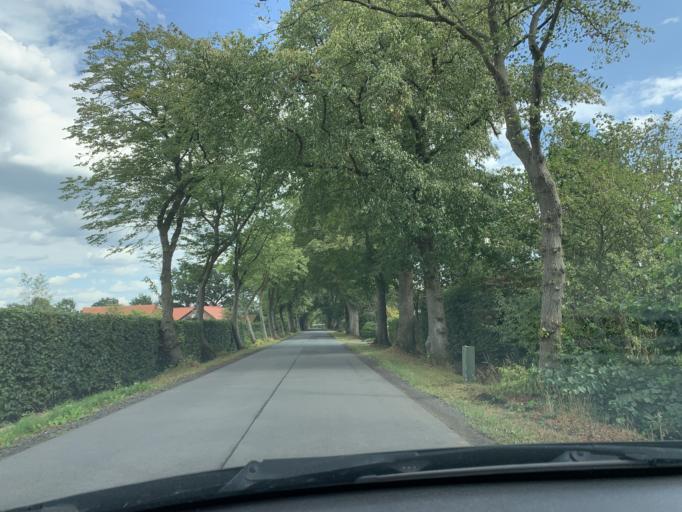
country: DE
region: Lower Saxony
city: Westerstede
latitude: 53.2552
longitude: 7.8800
